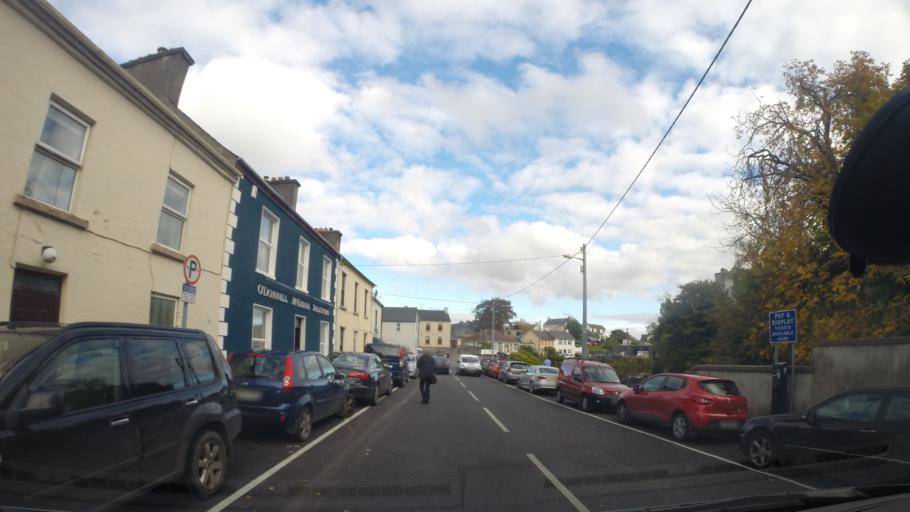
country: IE
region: Ulster
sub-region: County Donegal
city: Donegal
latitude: 54.6555
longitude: -8.1118
